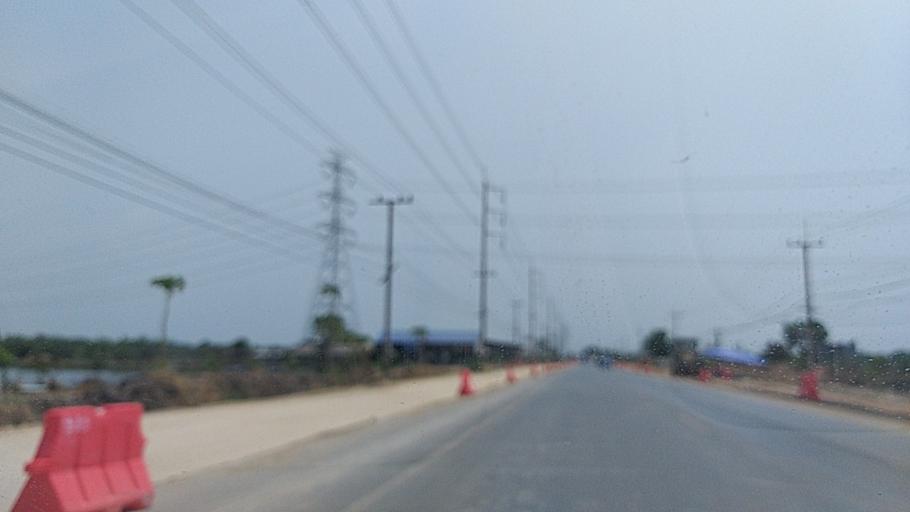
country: TH
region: Chachoengsao
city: Ban Pho
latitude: 13.5797
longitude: 101.1247
